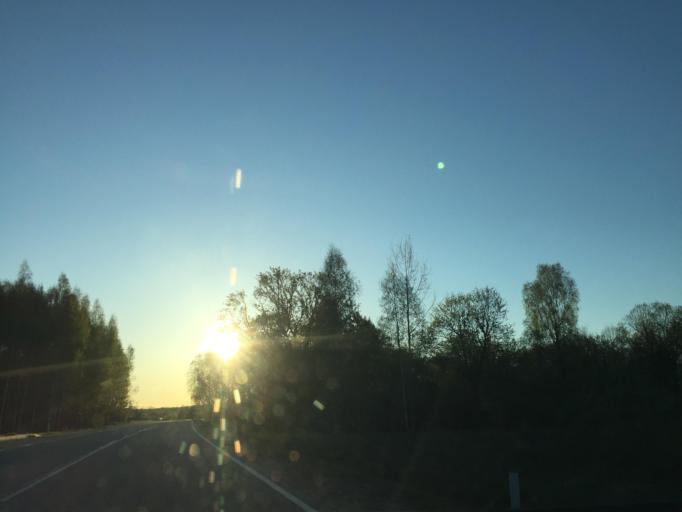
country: LV
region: Malpils
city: Malpils
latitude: 56.9248
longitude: 25.0292
